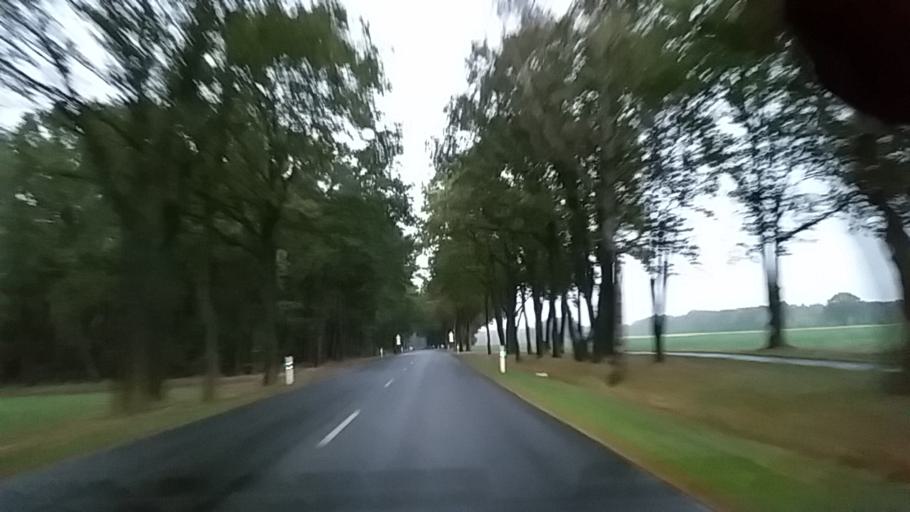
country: DE
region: Lower Saxony
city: Bokensdorf
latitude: 52.4831
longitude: 10.7162
